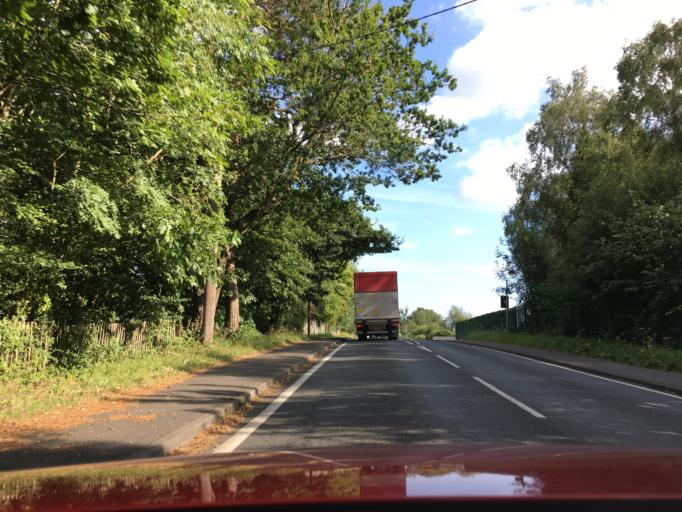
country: GB
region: England
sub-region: Hampshire
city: Colden Common
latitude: 50.9979
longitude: -1.3144
